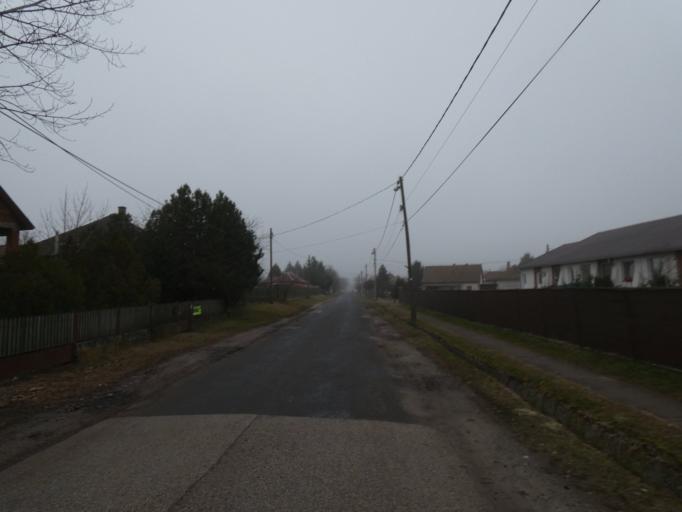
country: HU
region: Pest
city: Tapioszele
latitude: 47.3447
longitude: 19.8742
